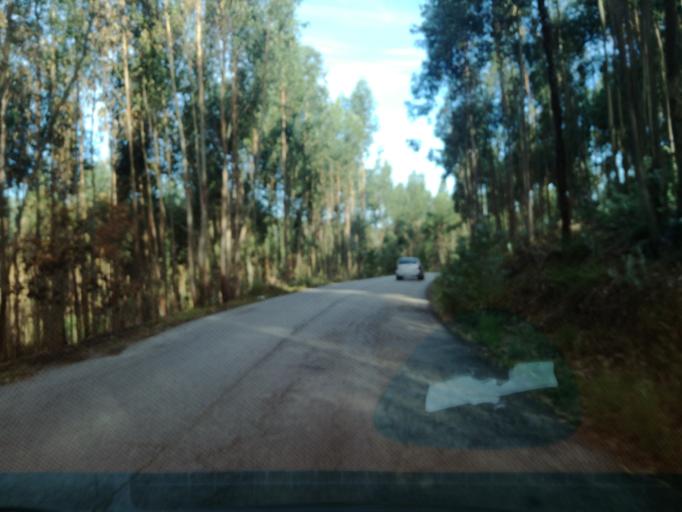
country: PT
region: Porto
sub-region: Valongo
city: Alfena
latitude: 41.2628
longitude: -8.5239
